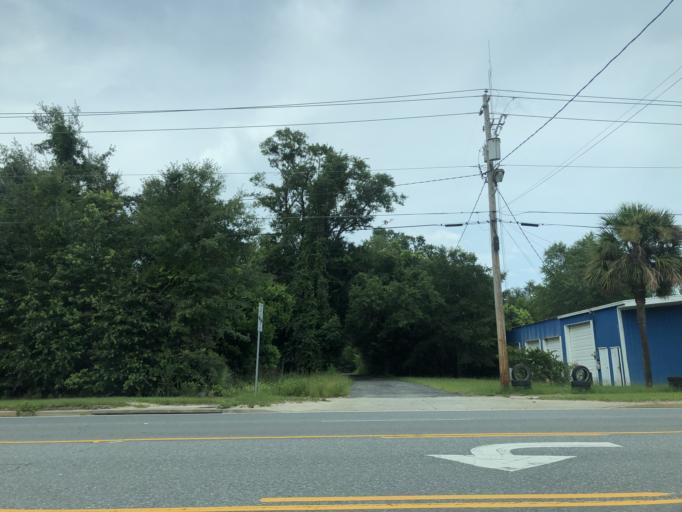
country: US
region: Georgia
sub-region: Wayne County
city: Jesup
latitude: 31.6007
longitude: -81.8728
